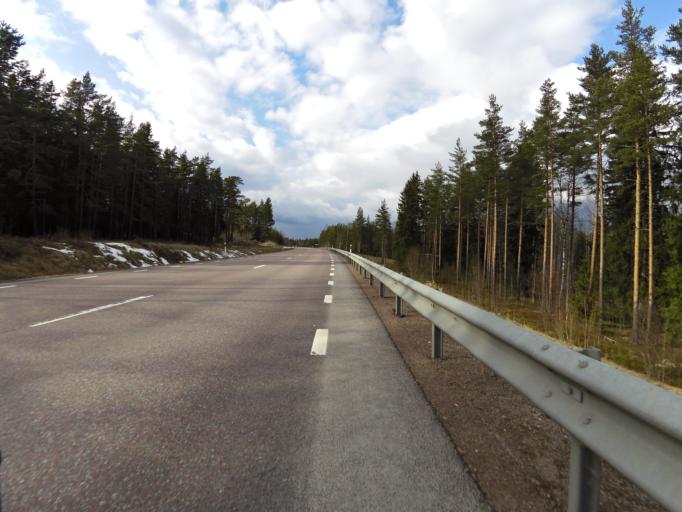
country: SE
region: Gaevleborg
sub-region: Hofors Kommun
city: Hofors
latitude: 60.4915
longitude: 16.4407
